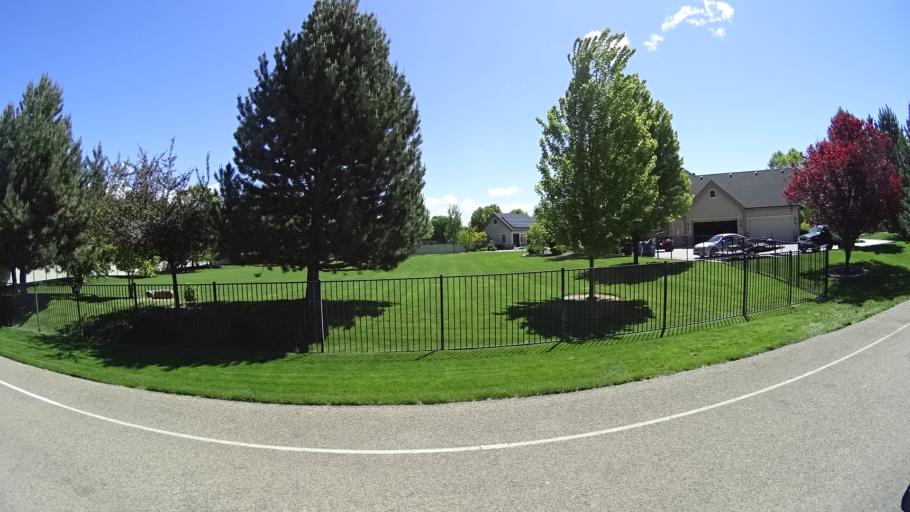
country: US
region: Idaho
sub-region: Ada County
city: Eagle
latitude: 43.6681
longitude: -116.3855
